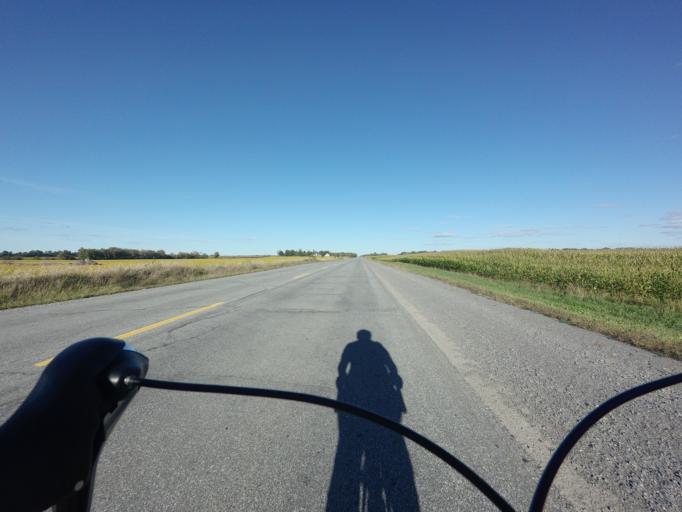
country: CA
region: Ontario
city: Bells Corners
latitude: 45.1838
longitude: -75.8005
